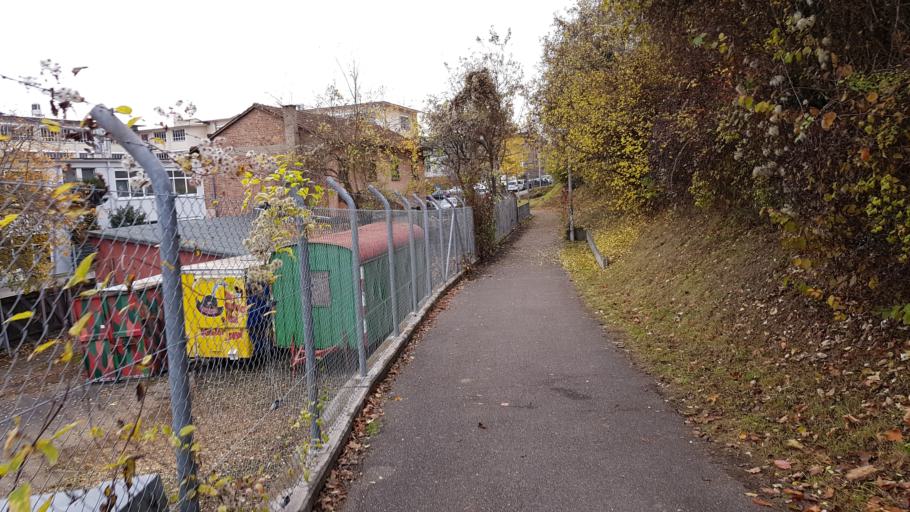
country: DE
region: Baden-Wuerttemberg
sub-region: Regierungsbezirk Stuttgart
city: Stuttgart-Ost
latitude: 48.8126
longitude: 9.2132
